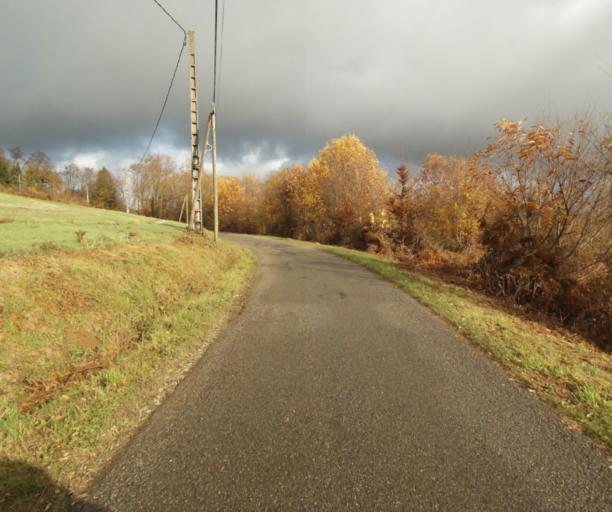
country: FR
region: Limousin
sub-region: Departement de la Correze
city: Sainte-Fereole
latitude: 45.2160
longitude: 1.6247
